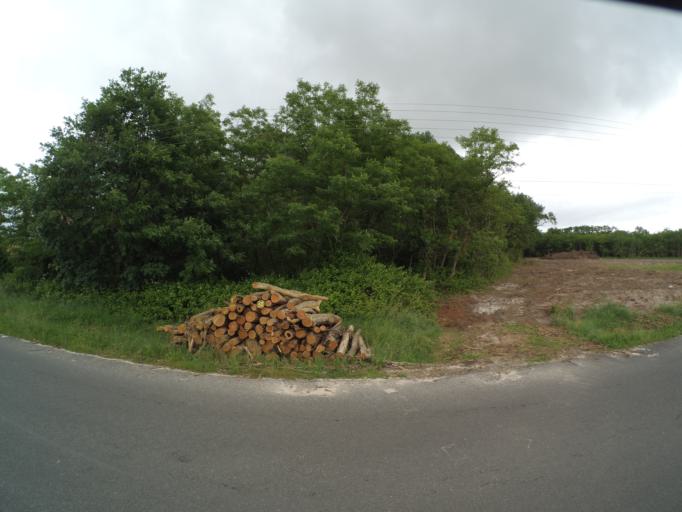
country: FR
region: Aquitaine
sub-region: Departement de la Gironde
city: Lamarque
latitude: 45.0881
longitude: -0.7265
